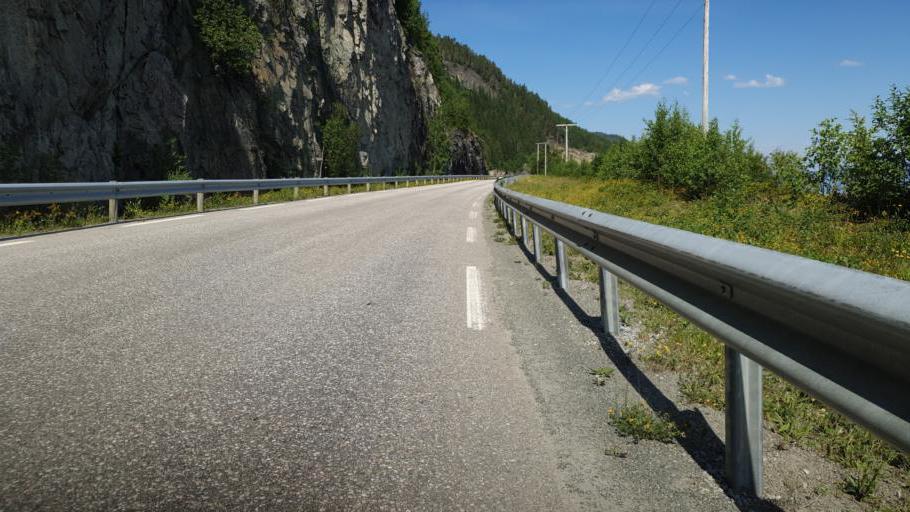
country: NO
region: Nord-Trondelag
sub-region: Leksvik
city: Leksvik
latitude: 63.6059
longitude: 10.4890
